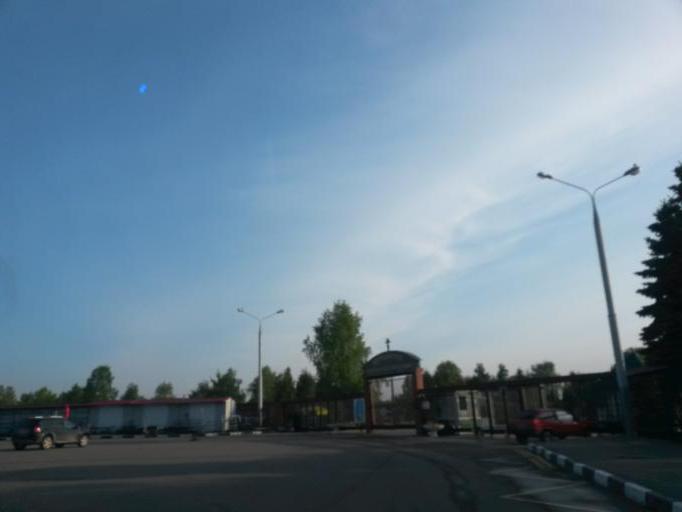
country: RU
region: Moskovskaya
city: Shcherbinka
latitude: 55.5057
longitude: 37.6179
